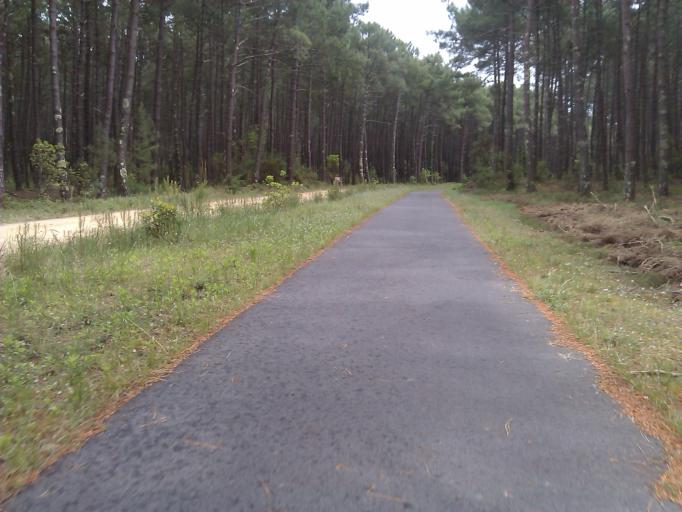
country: FR
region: Aquitaine
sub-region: Departement des Landes
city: Vielle-Saint-Girons
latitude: 43.9340
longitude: -1.3535
